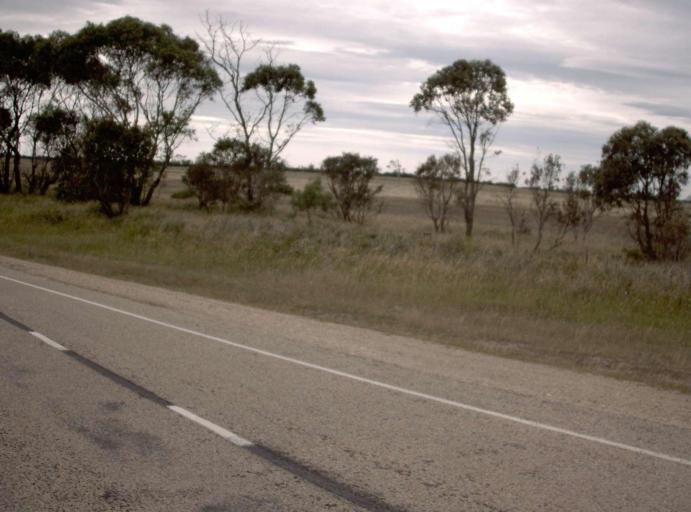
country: AU
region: Victoria
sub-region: East Gippsland
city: Bairnsdale
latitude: -37.9501
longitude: 147.5199
